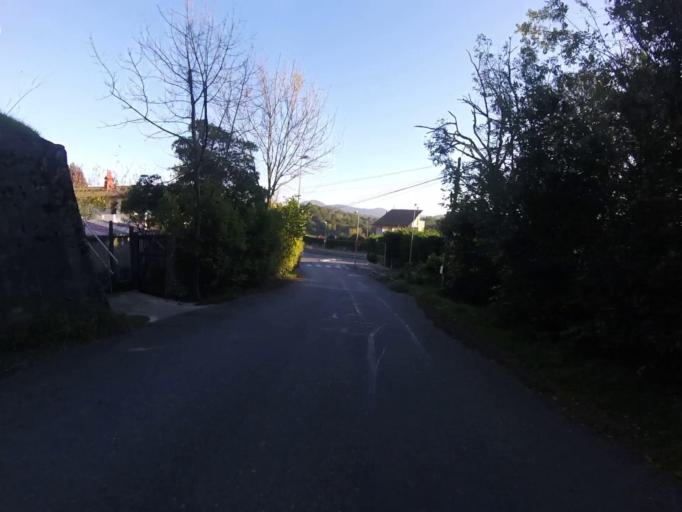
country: ES
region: Basque Country
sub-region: Provincia de Guipuzcoa
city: Lasarte
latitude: 43.2812
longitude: -2.0083
